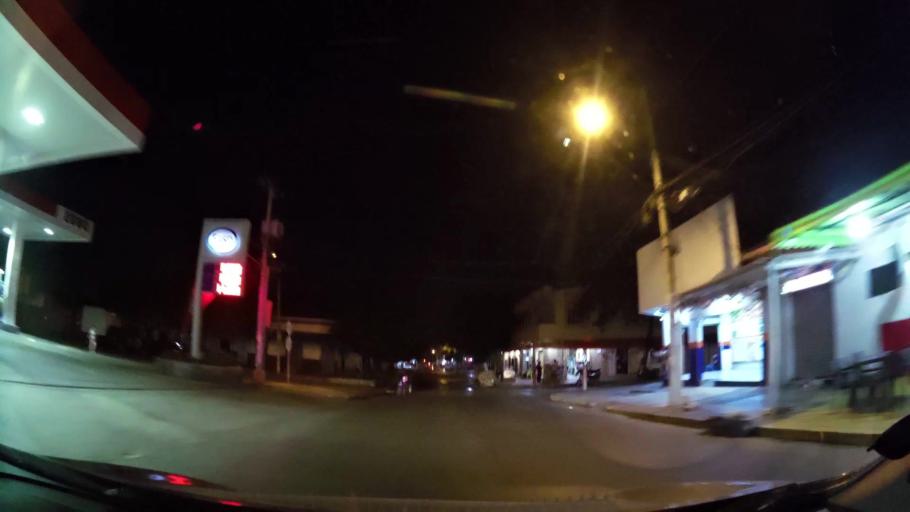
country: CO
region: Atlantico
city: Barranquilla
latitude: 10.9648
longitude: -74.7869
